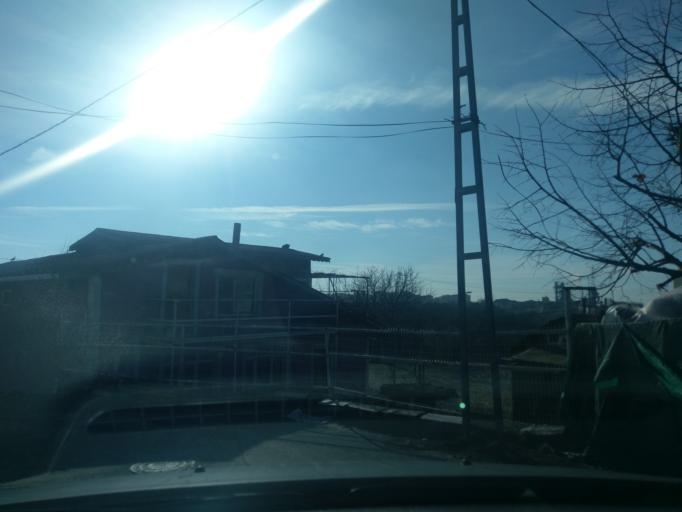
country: TR
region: Istanbul
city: Sultangazi
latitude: 41.1318
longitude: 28.8462
